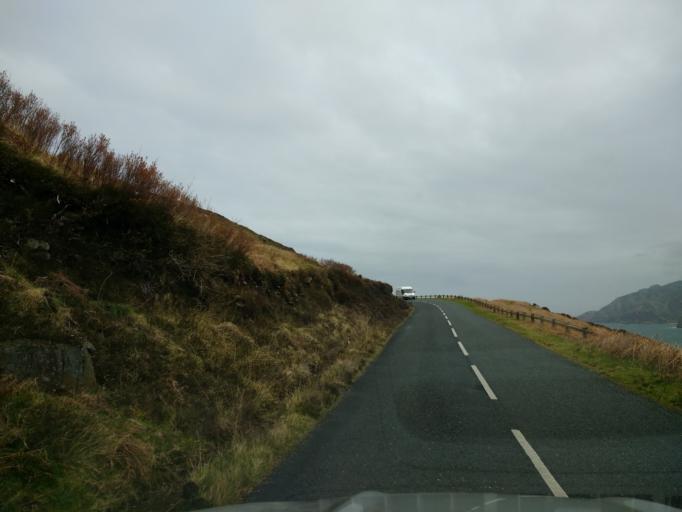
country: IE
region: Ulster
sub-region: County Donegal
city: Buncrana
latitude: 55.1789
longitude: -7.5781
